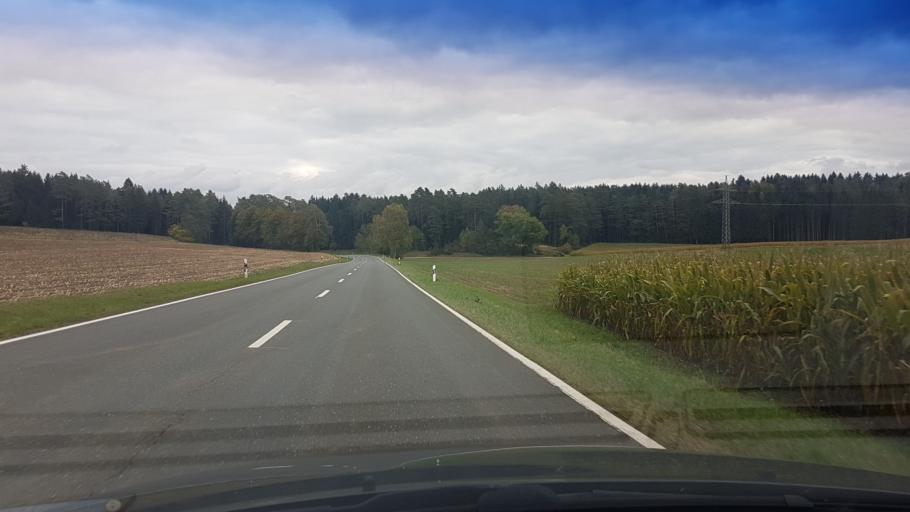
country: DE
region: Bavaria
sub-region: Upper Franconia
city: Stadelhofen
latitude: 50.0104
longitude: 11.2147
